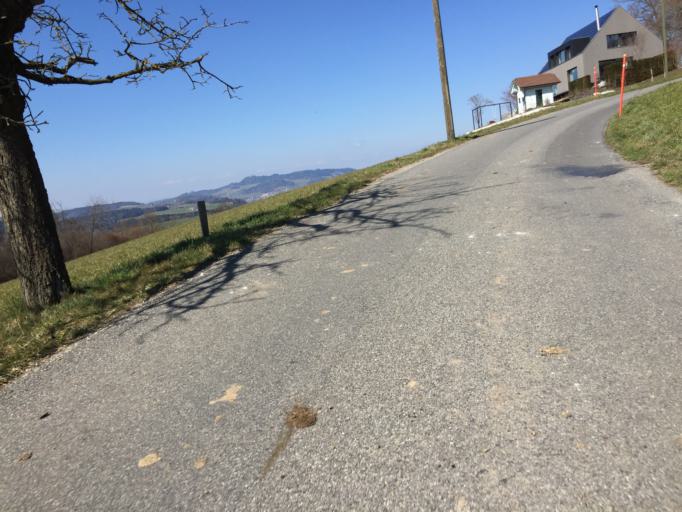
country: CH
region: Bern
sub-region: Bern-Mittelland District
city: Taegertschi
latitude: 46.8949
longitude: 7.5831
